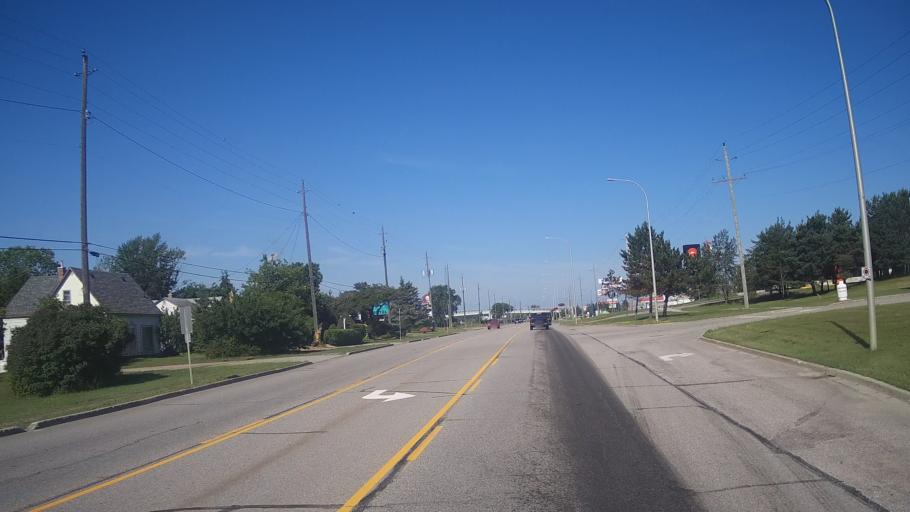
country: CA
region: Ontario
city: Dryden
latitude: 49.7864
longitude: -92.8279
